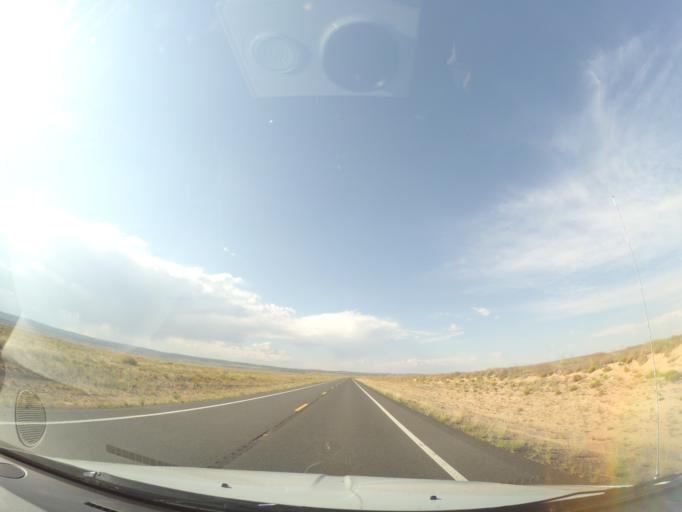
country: US
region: Arizona
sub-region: Coconino County
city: Tuba City
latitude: 36.4054
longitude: -111.4223
